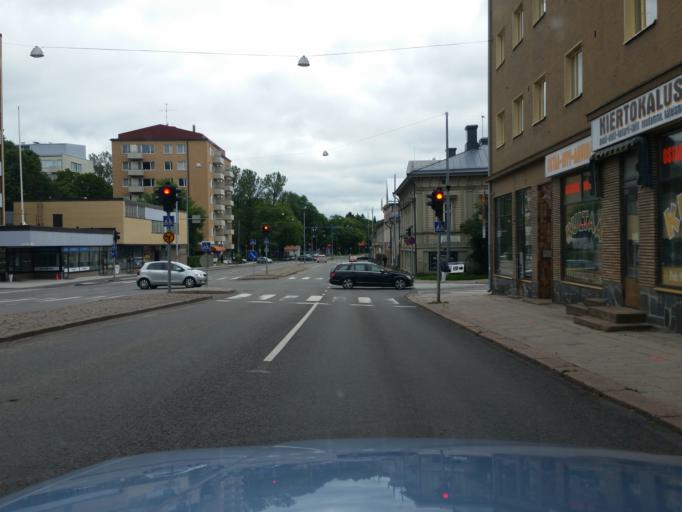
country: FI
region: Varsinais-Suomi
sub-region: Turku
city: Turku
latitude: 60.4477
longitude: 22.2817
